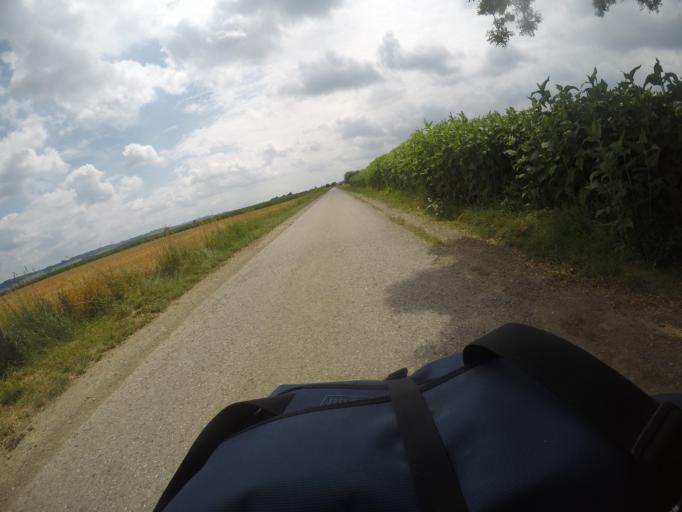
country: DE
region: Bavaria
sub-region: Swabia
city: Fellheim
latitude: 48.0854
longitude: 10.1560
